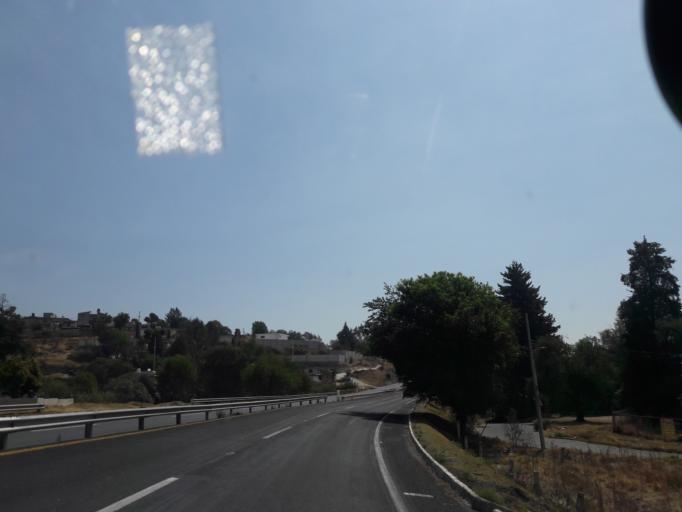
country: MX
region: Tlaxcala
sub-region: Totolac
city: La Candelaria Teotlalpan
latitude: 19.3374
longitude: -98.2156
